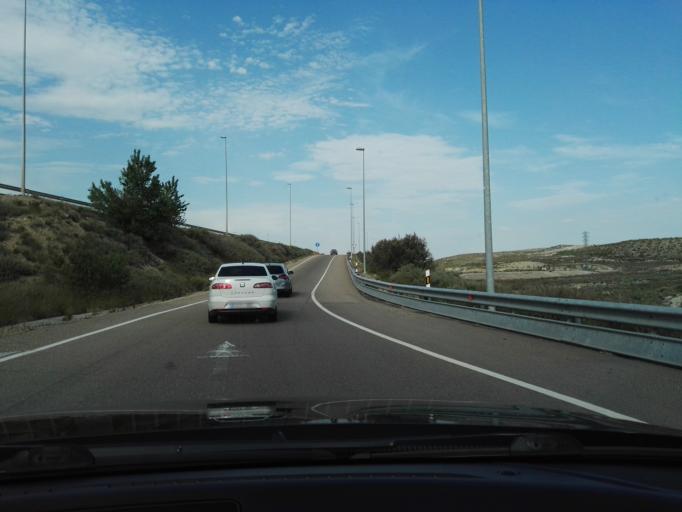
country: ES
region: Aragon
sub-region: Provincia de Zaragoza
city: Montecanal
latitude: 41.6183
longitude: -0.9602
